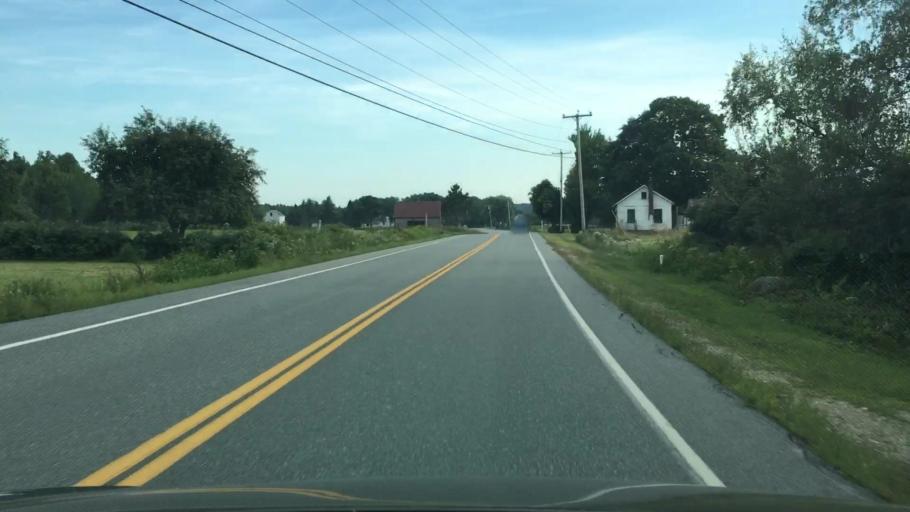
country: US
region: Maine
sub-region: Hancock County
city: Penobscot
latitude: 44.4665
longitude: -68.7819
